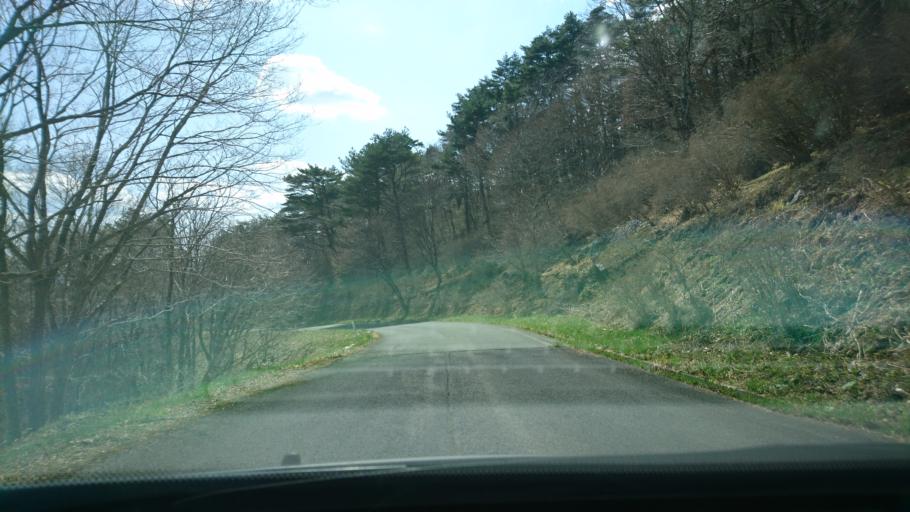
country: JP
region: Iwate
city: Ofunato
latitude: 38.9694
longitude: 141.4547
